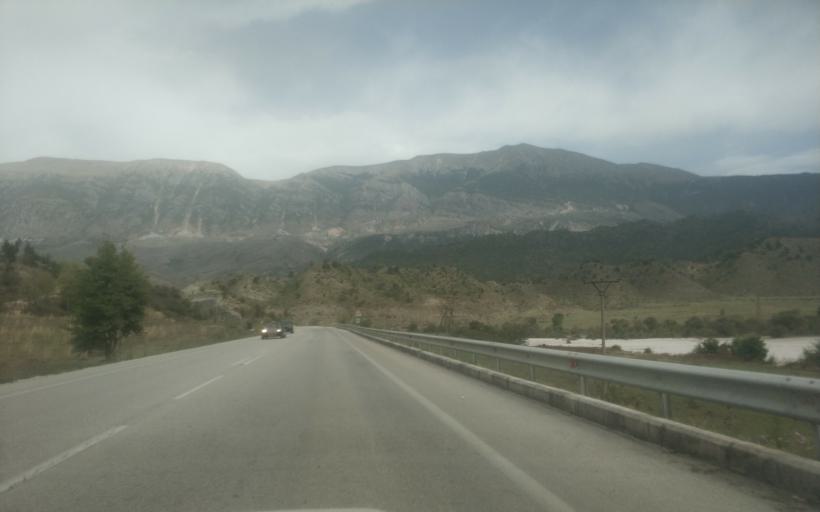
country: AL
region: Gjirokaster
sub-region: Rrethi i Gjirokastres
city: Picar
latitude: 40.2001
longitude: 20.0889
